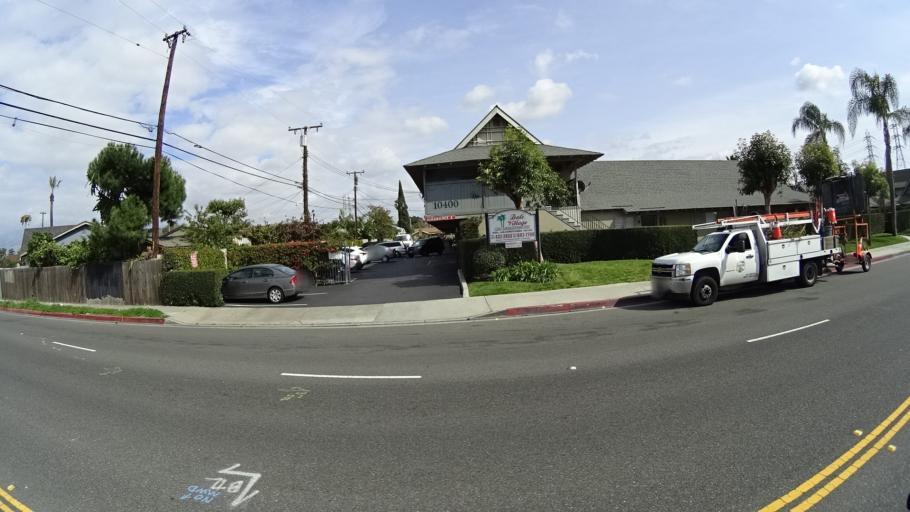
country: US
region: California
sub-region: Orange County
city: Stanton
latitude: 33.8120
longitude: -117.9846
